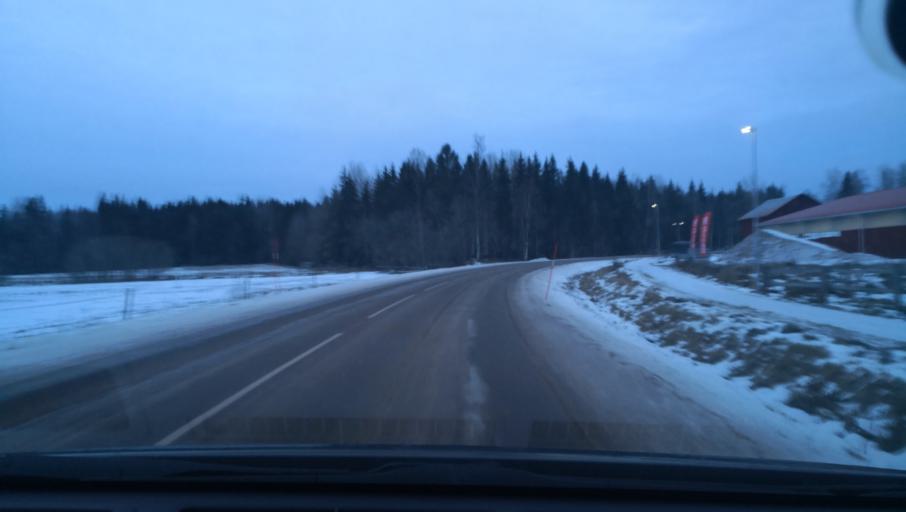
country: SE
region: Dalarna
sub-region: Avesta Kommun
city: Horndal
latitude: 60.1986
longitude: 16.4616
